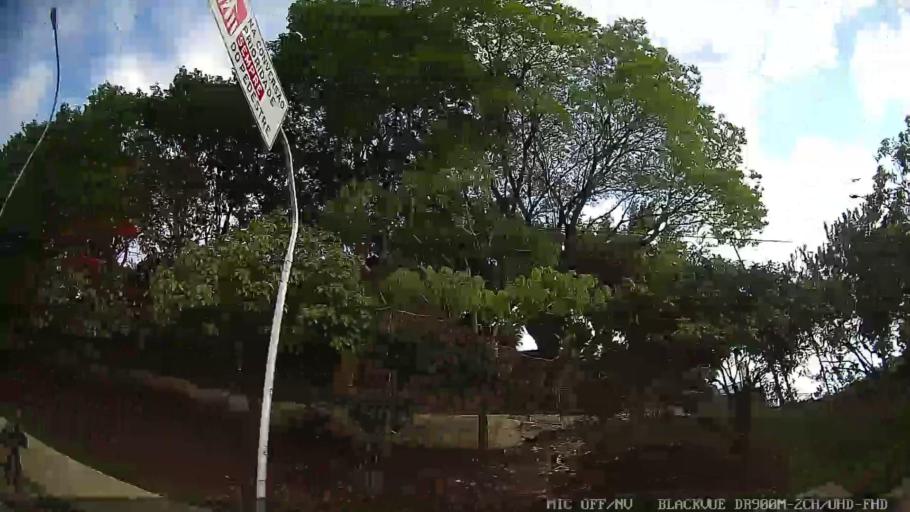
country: BR
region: Sao Paulo
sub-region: Guarulhos
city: Guarulhos
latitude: -23.5323
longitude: -46.5298
